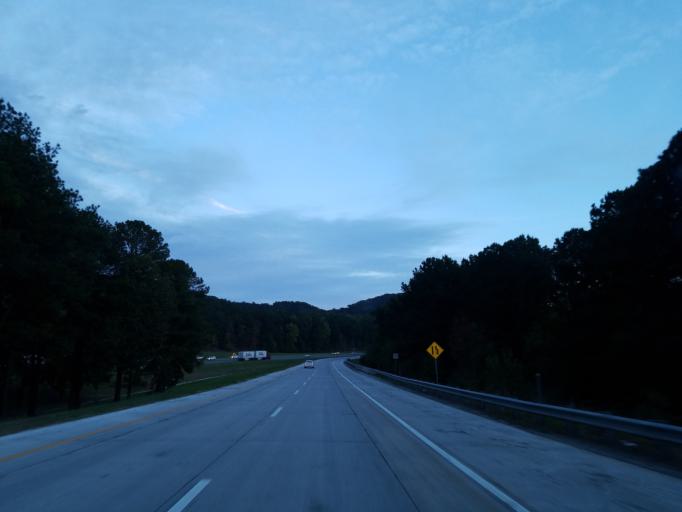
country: US
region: Georgia
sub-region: Bartow County
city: Emerson
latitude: 34.1413
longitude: -84.7398
